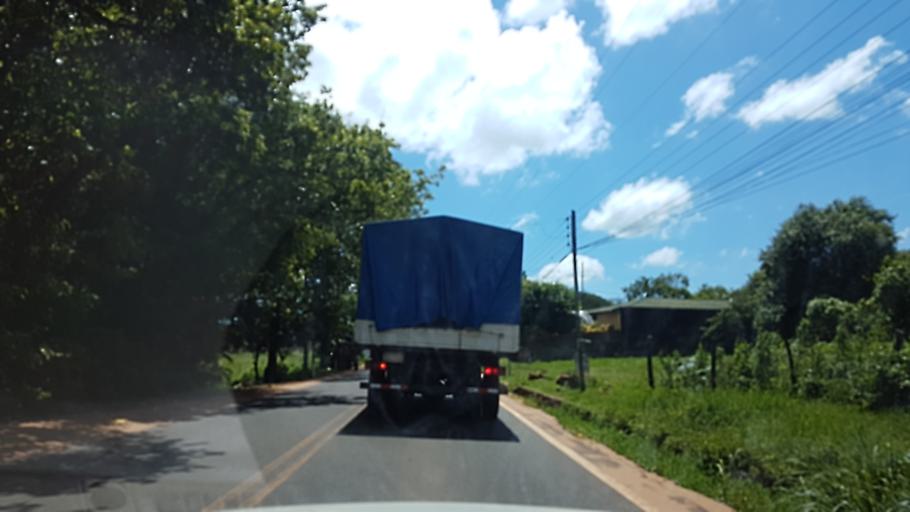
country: PY
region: Central
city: Capiata
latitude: -25.3243
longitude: -57.4584
